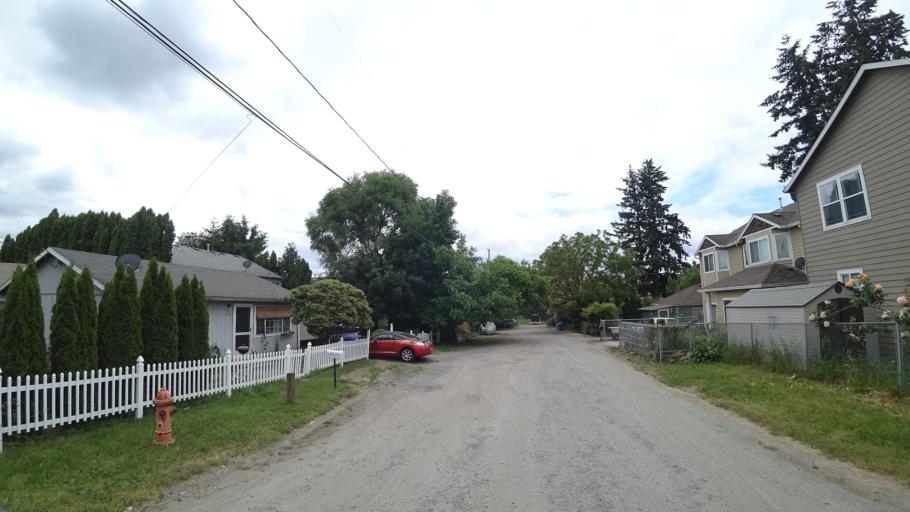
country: US
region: Oregon
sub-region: Multnomah County
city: Lents
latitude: 45.5033
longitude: -122.5755
